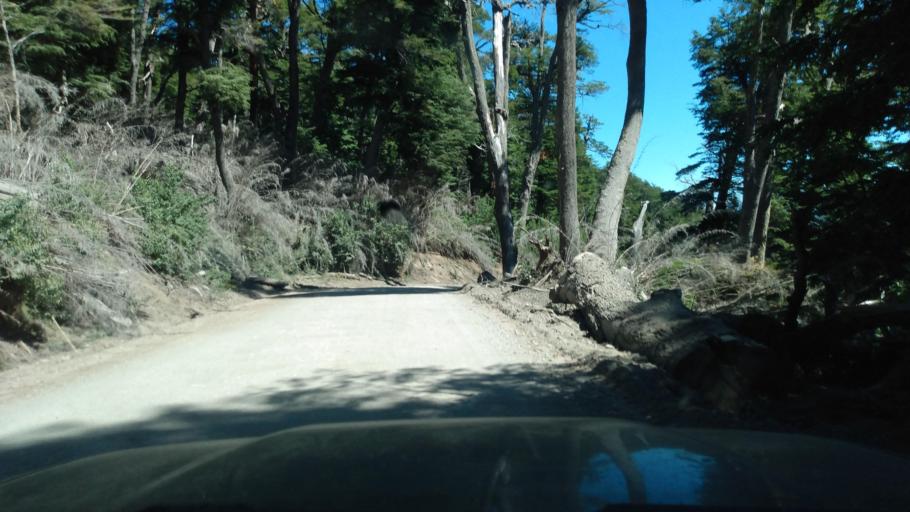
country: AR
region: Neuquen
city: Villa La Angostura
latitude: -40.6094
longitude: -71.6434
